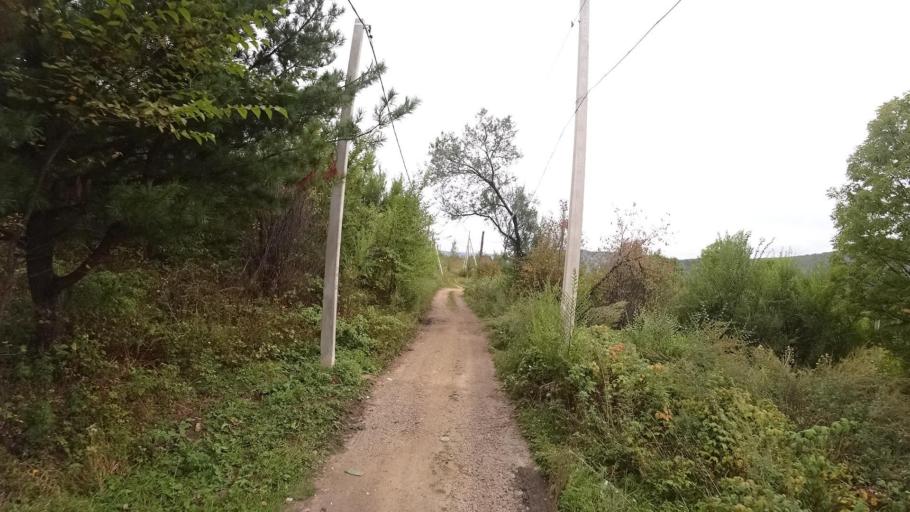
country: RU
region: Jewish Autonomous Oblast
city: Khingansk
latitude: 49.0312
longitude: 131.0600
